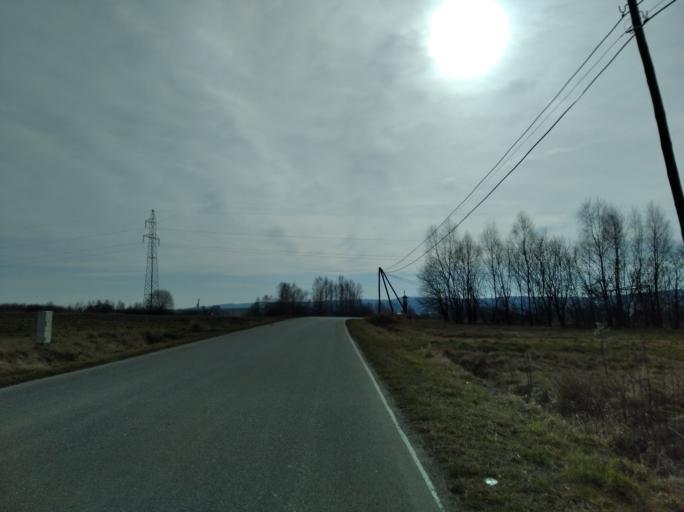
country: PL
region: Subcarpathian Voivodeship
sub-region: Powiat brzozowski
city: Jasienica Rosielna
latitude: 49.7435
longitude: 21.9426
